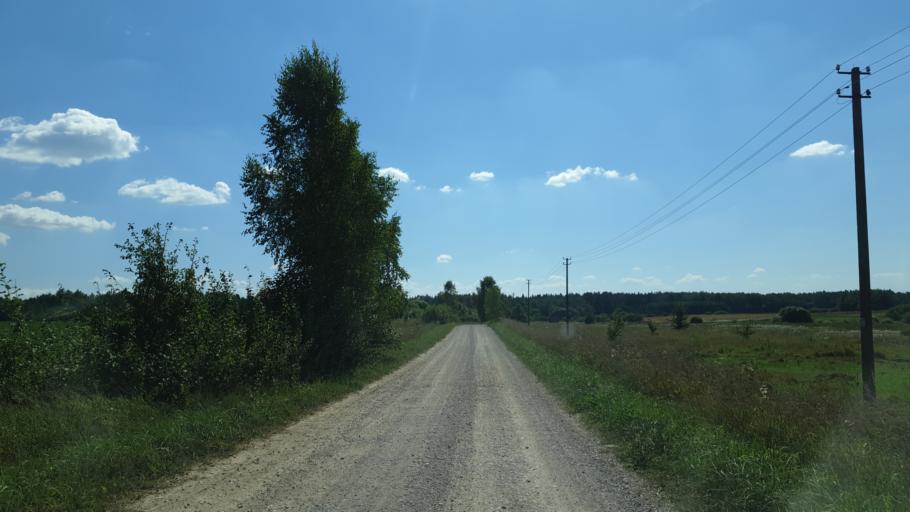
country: LT
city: Sirvintos
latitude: 54.9061
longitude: 24.9110
